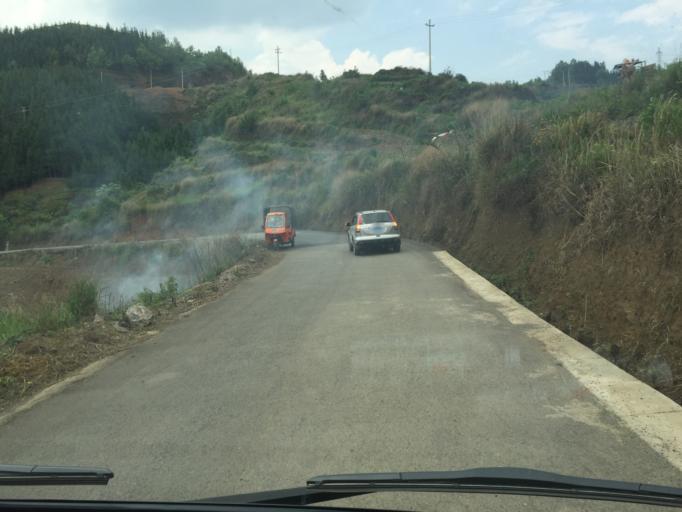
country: CN
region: Guangxi Zhuangzu Zizhiqu
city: Xinzhou
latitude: 25.6560
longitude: 105.2373
